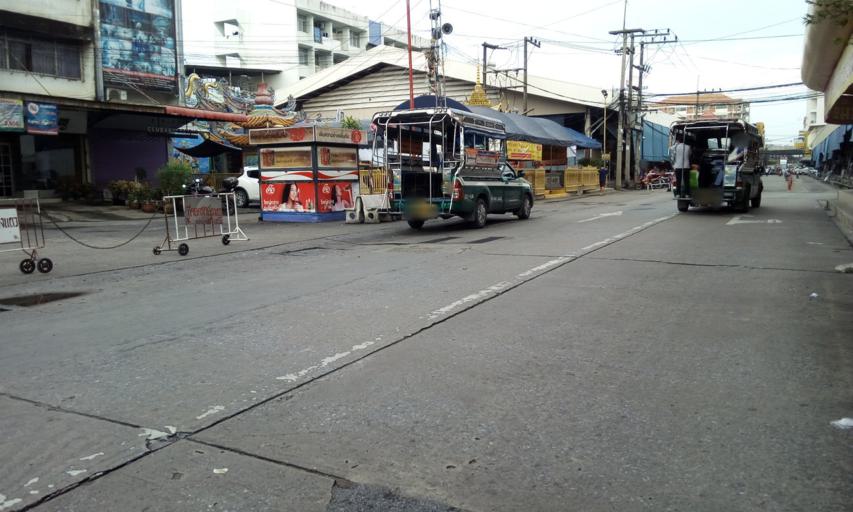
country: TH
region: Phra Nakhon Si Ayutthaya
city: Ban Bang Kadi Pathum Thani
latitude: 13.9851
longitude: 100.6140
